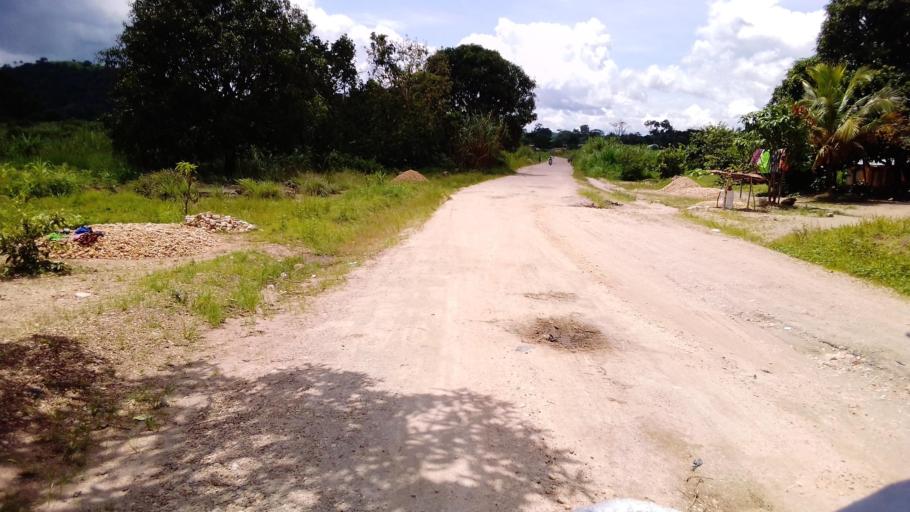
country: SL
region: Eastern Province
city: Koidu
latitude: 8.6729
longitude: -10.9918
